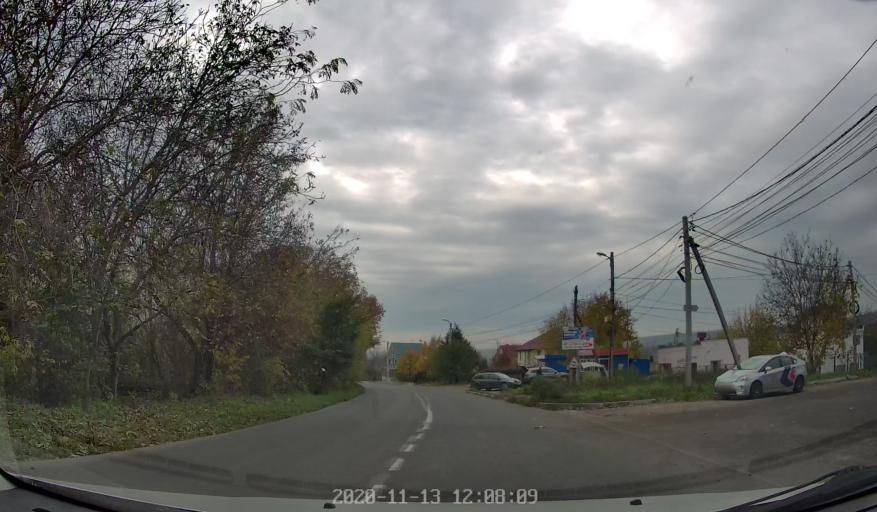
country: MD
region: Chisinau
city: Chisinau
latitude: 46.9683
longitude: 28.8335
